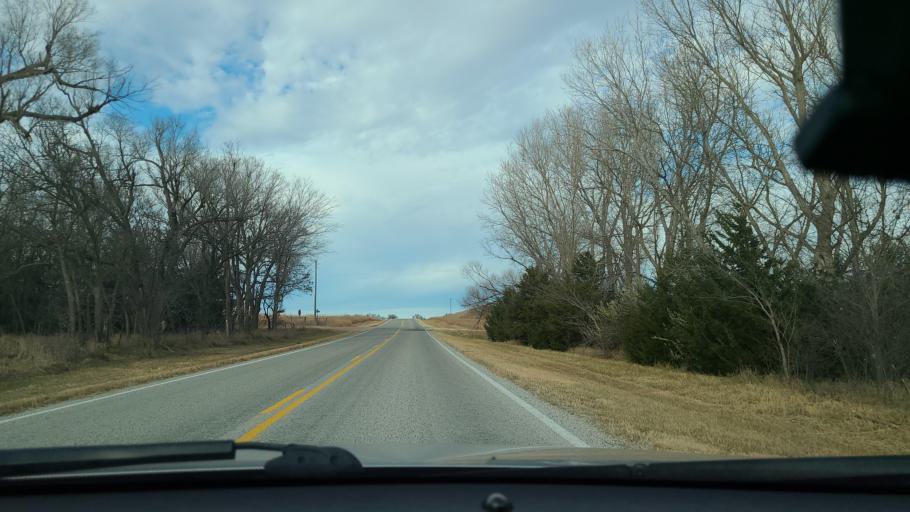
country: US
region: Kansas
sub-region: McPherson County
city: Inman
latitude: 38.3470
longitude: -97.9244
